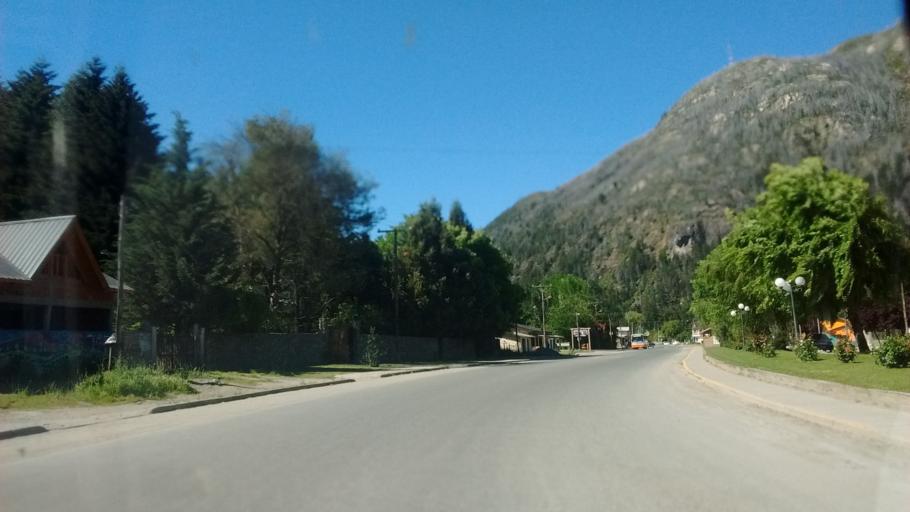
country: AR
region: Chubut
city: Lago Puelo
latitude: -42.0600
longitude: -71.6003
